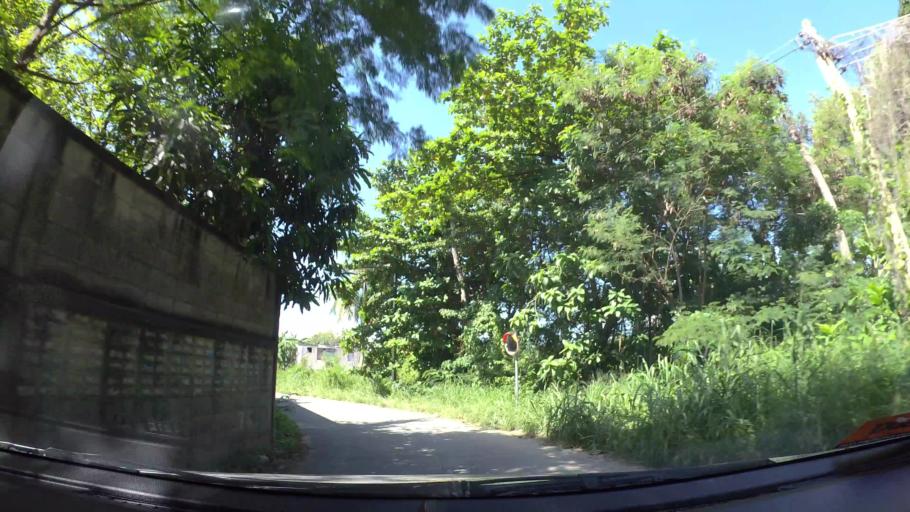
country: TH
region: Chon Buri
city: Si Racha
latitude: 13.1620
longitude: 100.9345
